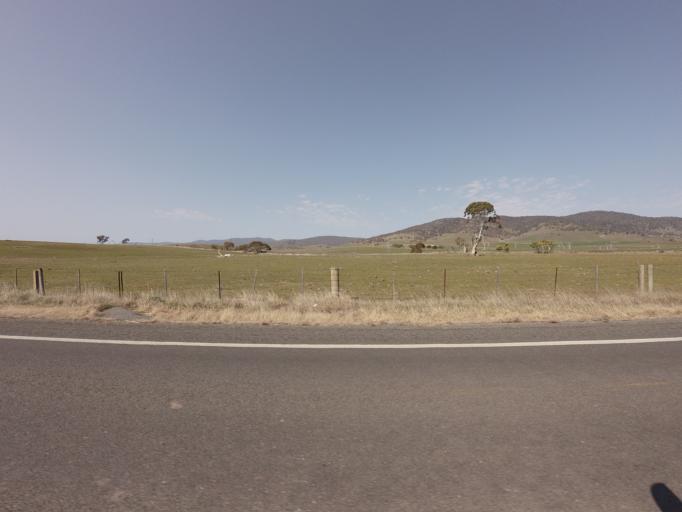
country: AU
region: Tasmania
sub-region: Northern Midlands
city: Evandale
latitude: -41.8086
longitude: 147.6727
